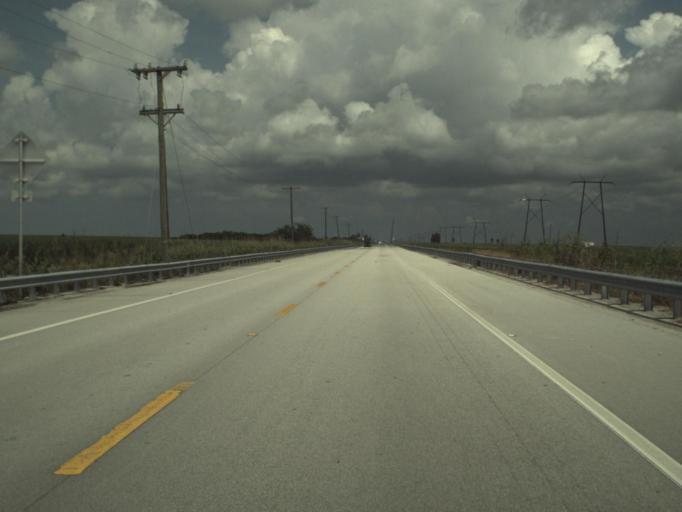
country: US
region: Florida
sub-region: Palm Beach County
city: Pahokee
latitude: 26.7516
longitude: -80.4824
